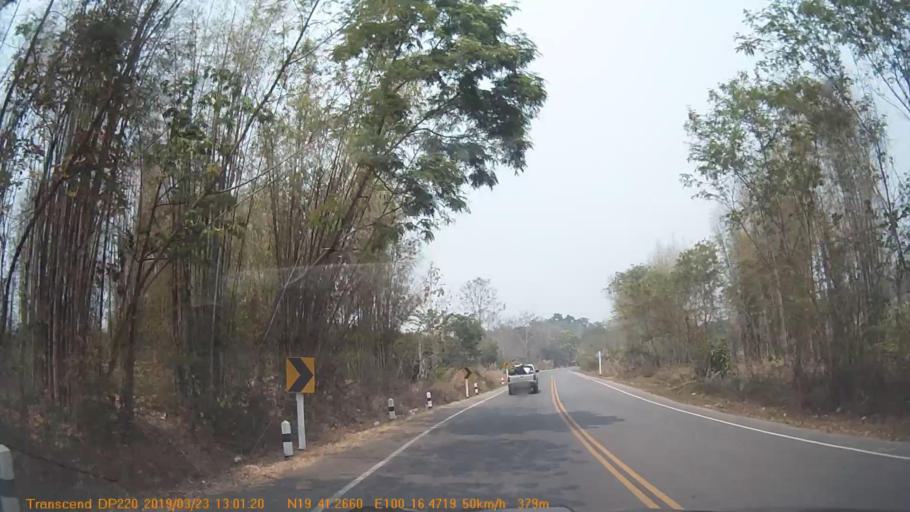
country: TH
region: Chiang Rai
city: Thoeng
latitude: 19.6881
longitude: 100.2745
